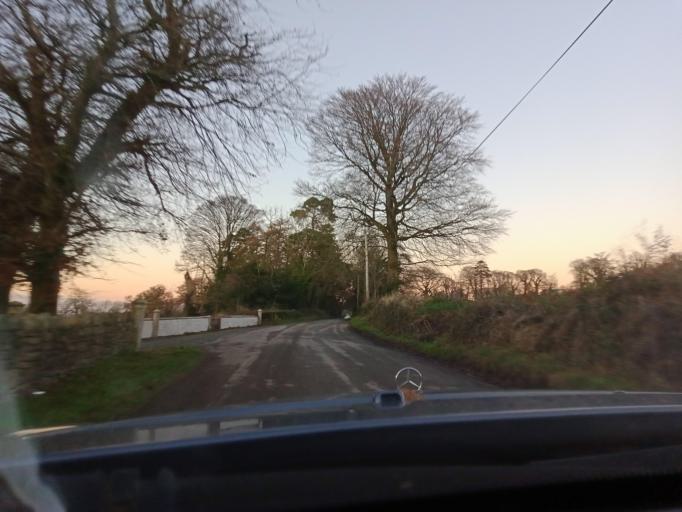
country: IE
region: Leinster
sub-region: Kilkenny
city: Thomastown
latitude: 52.4617
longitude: -7.1019
